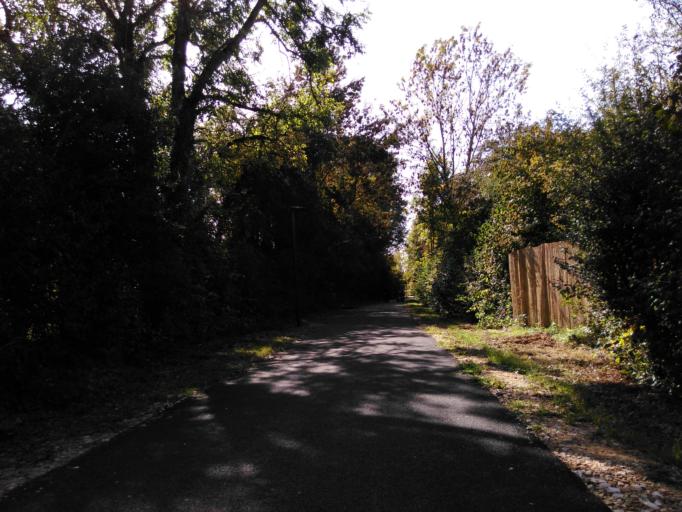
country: LU
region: Luxembourg
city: Tetange
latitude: 49.4710
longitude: 6.0391
